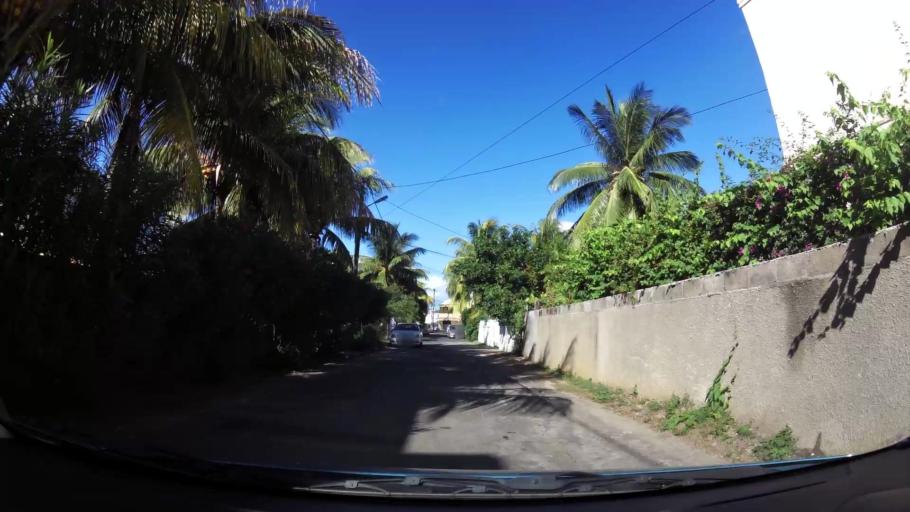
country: MU
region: Black River
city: Grande Riviere Noire
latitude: -20.3515
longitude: 57.3633
